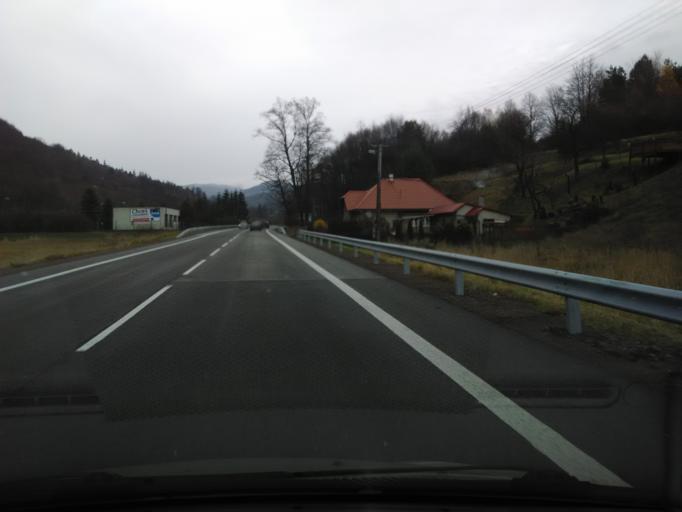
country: SK
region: Banskobystricky
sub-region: Okres Ziar nad Hronom
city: Kremnica
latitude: 48.6691
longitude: 18.9105
